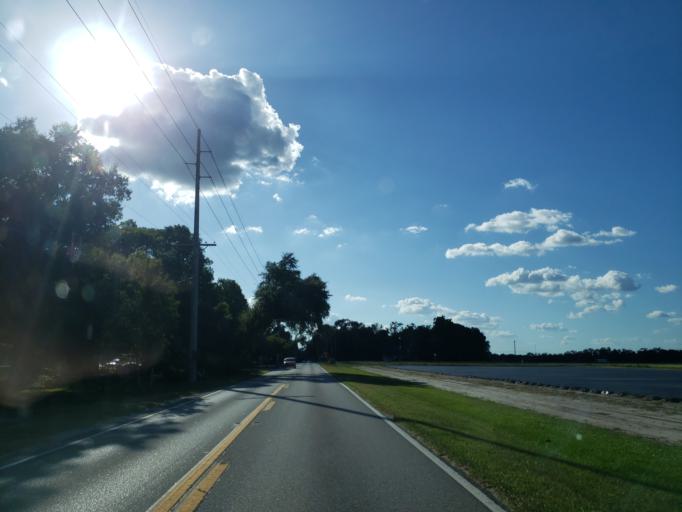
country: US
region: Florida
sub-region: Hillsborough County
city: Dover
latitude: 27.9671
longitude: -82.2047
